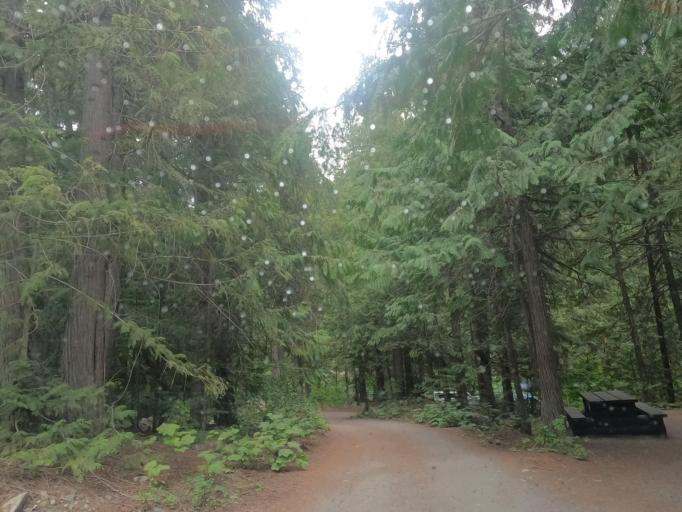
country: CA
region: British Columbia
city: Lillooet
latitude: 50.5290
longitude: -122.1570
